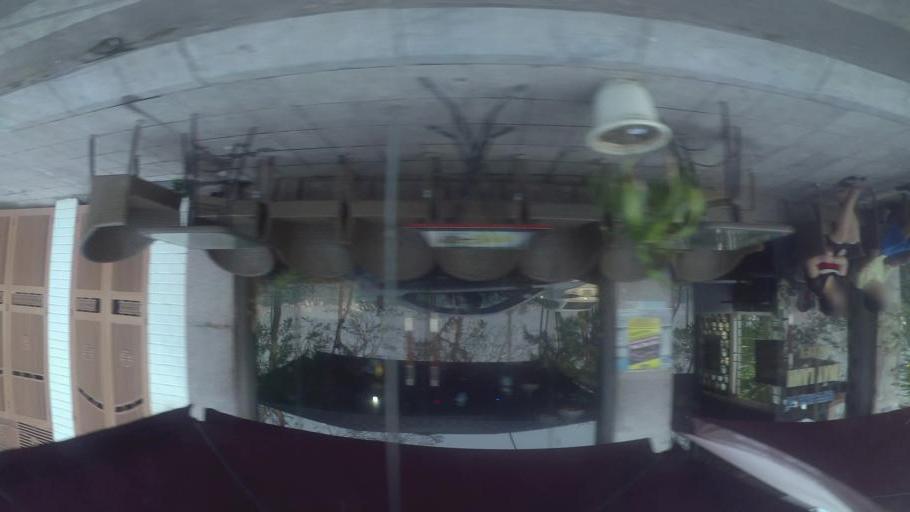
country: VN
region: Ha Noi
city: Tay Ho
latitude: 21.0636
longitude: 105.8102
